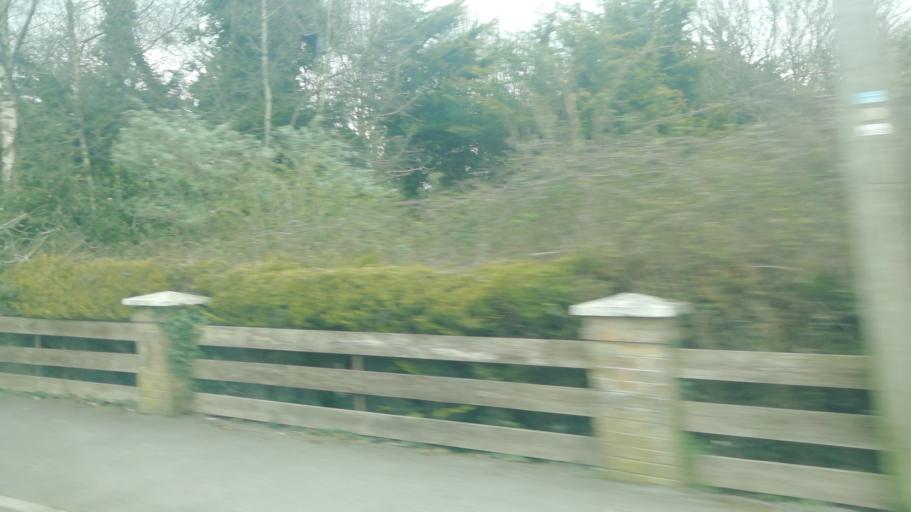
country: IE
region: Leinster
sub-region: Kildare
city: Prosperous
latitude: 53.2903
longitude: -6.7532
